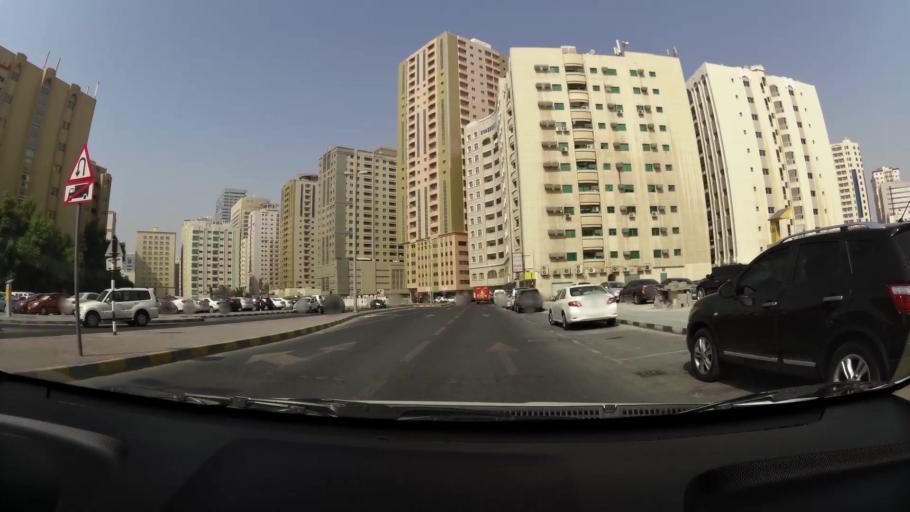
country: AE
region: Ash Shariqah
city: Sharjah
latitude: 25.3426
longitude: 55.3887
